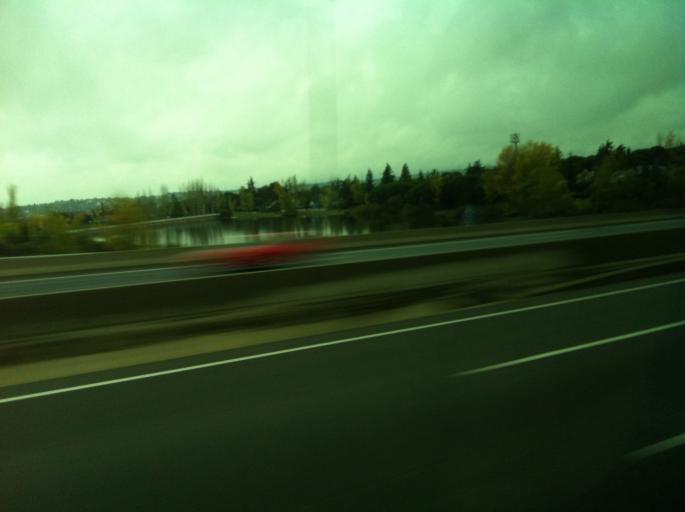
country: ES
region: Madrid
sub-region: Provincia de Madrid
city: Galapagar
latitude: 40.6031
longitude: -3.9651
